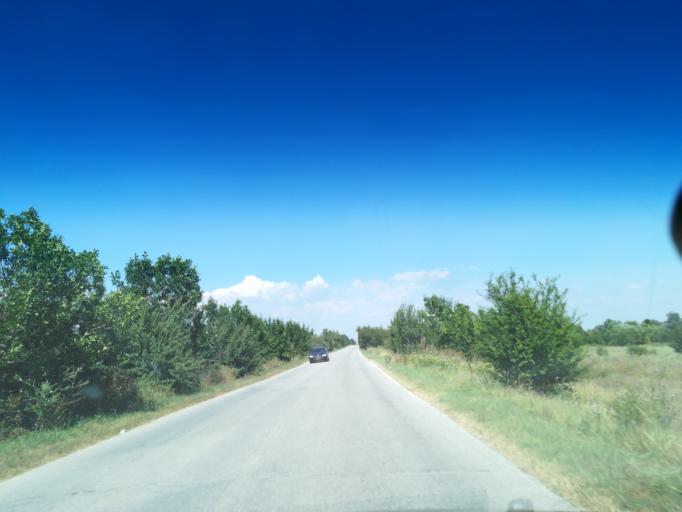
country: BG
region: Plovdiv
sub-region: Obshtina Sadovo
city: Sadovo
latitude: 42.0486
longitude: 25.1434
